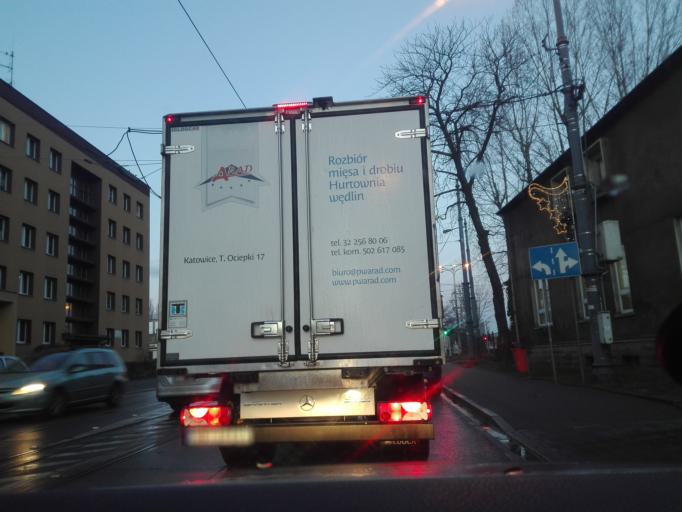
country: PL
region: Silesian Voivodeship
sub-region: Katowice
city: Katowice
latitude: 50.2671
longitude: 18.9910
